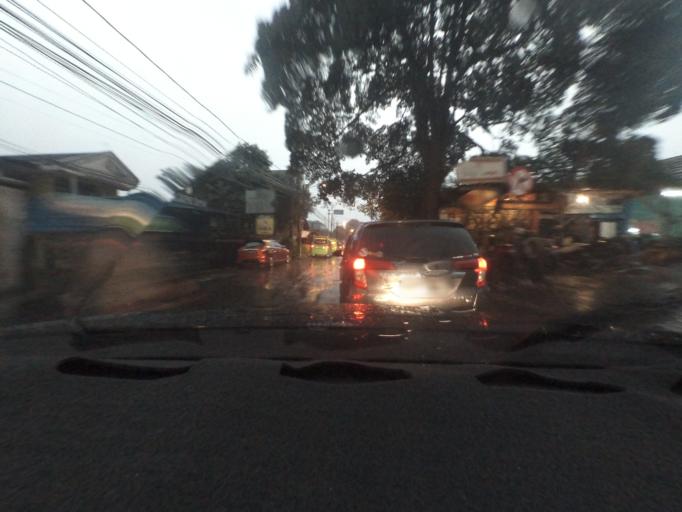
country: ID
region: West Java
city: Bogor
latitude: -6.5923
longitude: 106.7861
